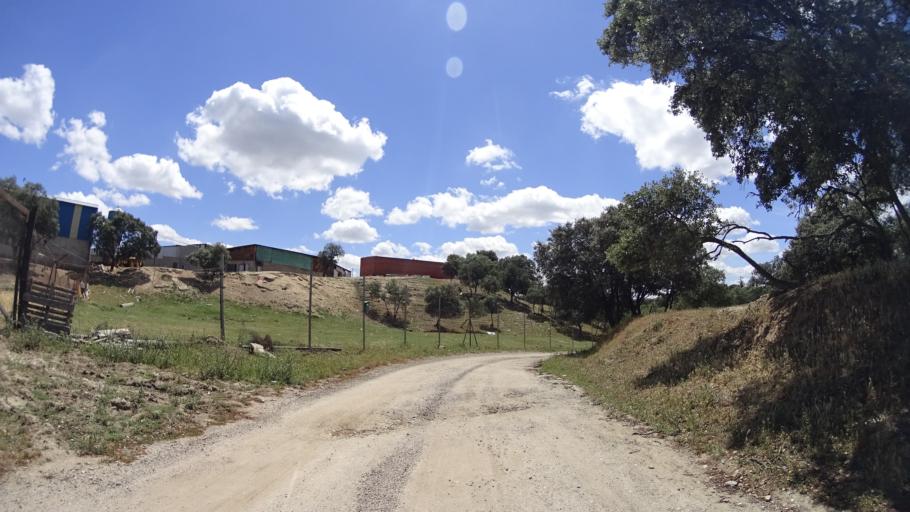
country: ES
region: Madrid
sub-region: Provincia de Madrid
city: Brunete
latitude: 40.4271
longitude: -3.9696
